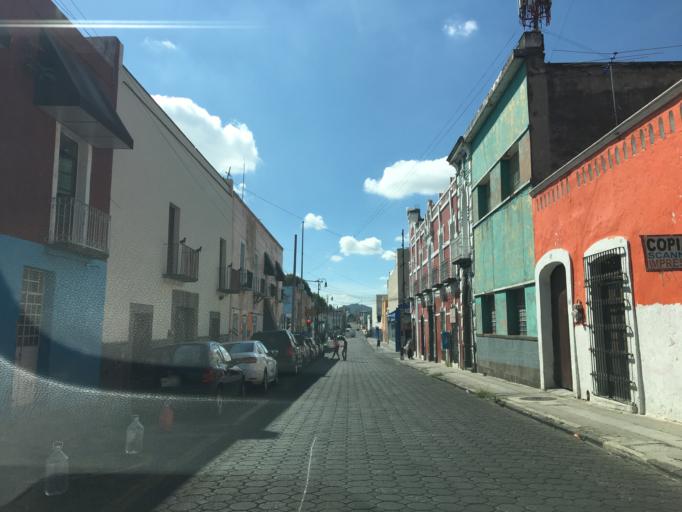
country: MX
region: Puebla
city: Puebla
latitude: 19.0402
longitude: -98.1979
